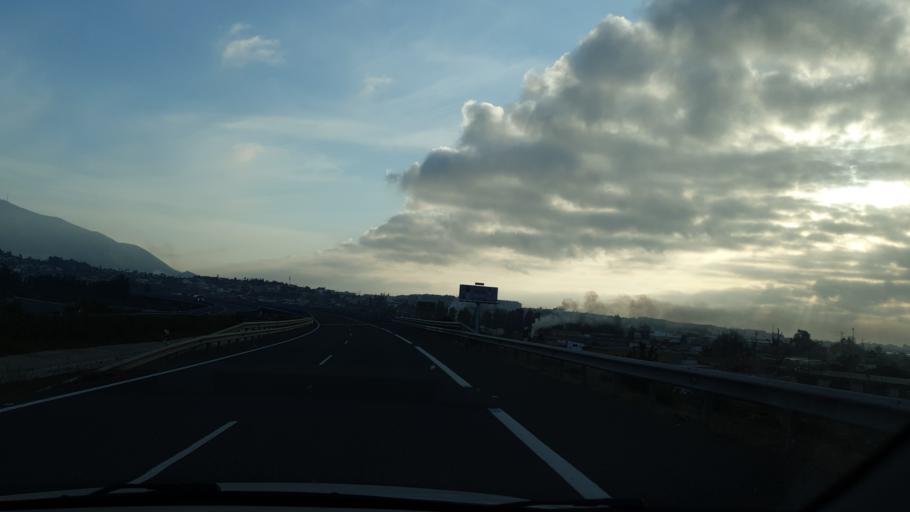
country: ES
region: Andalusia
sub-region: Provincia de Malaga
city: Fuengirola
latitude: 36.5409
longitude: -4.6625
